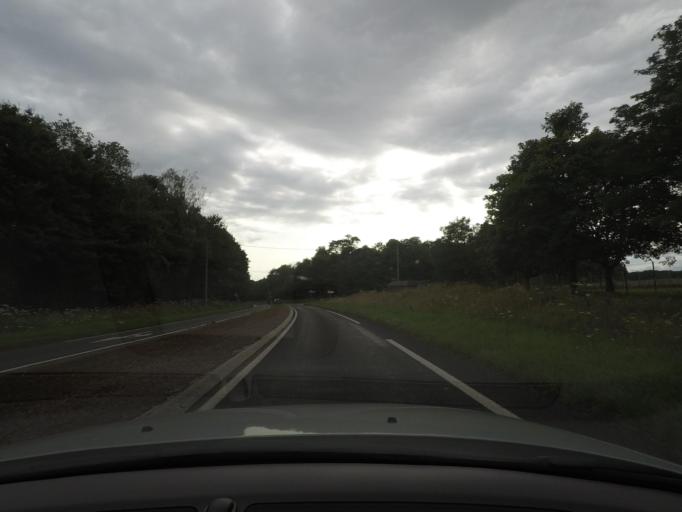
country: FR
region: Haute-Normandie
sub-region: Departement de la Seine-Maritime
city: Ymare
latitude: 49.3553
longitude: 1.1733
